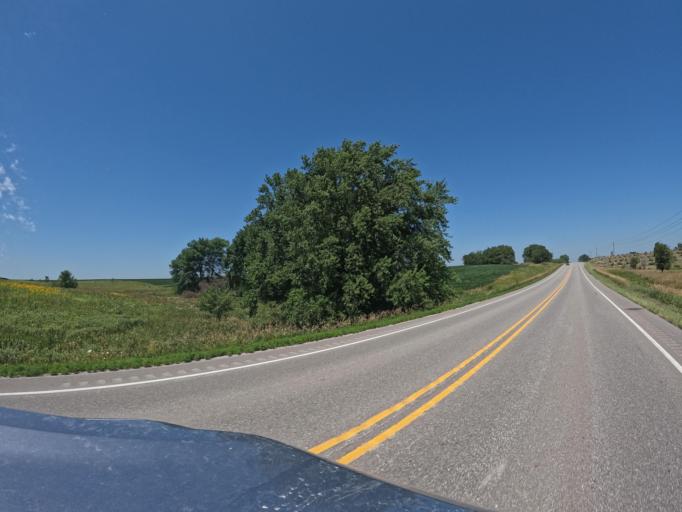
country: US
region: Iowa
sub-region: Keokuk County
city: Sigourney
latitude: 41.4602
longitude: -92.3551
